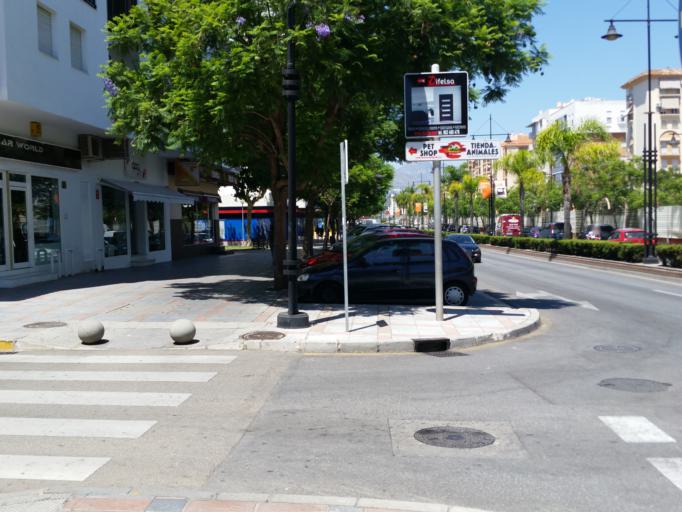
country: ES
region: Andalusia
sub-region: Provincia de Malaga
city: Fuengirola
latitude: 36.5463
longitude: -4.6209
